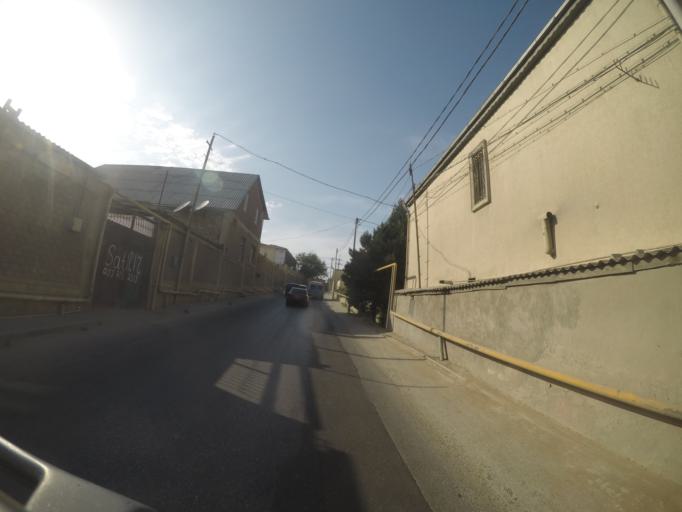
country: AZ
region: Baki
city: Binagadi
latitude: 40.4662
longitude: 49.8420
